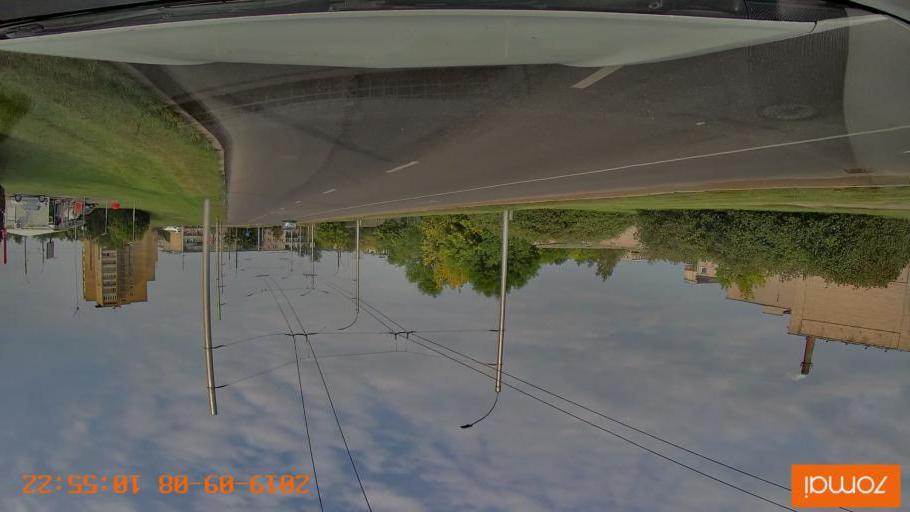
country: LT
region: Kauno apskritis
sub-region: Kaunas
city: Kaunas
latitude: 54.9134
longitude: 23.9063
